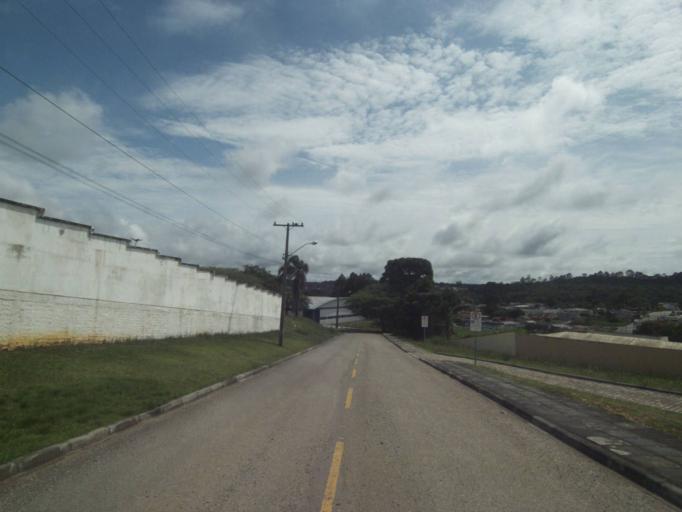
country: BR
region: Parana
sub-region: Campina Grande Do Sul
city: Campina Grande do Sul
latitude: -25.3078
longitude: -49.0579
